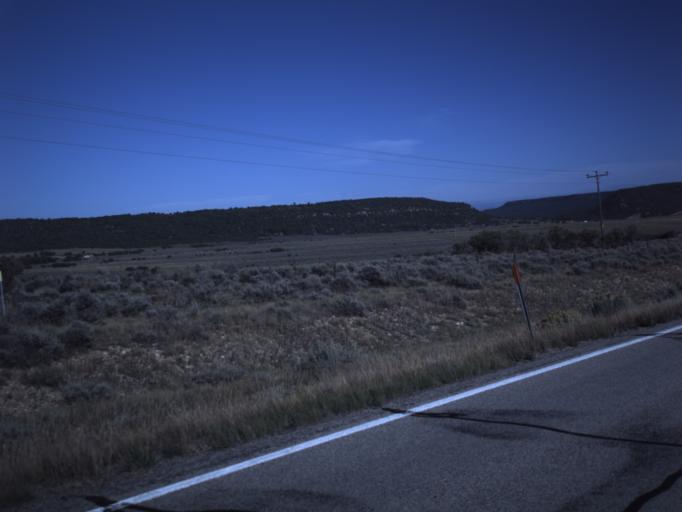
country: US
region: Utah
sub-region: Grand County
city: Moab
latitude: 38.3369
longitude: -109.1616
